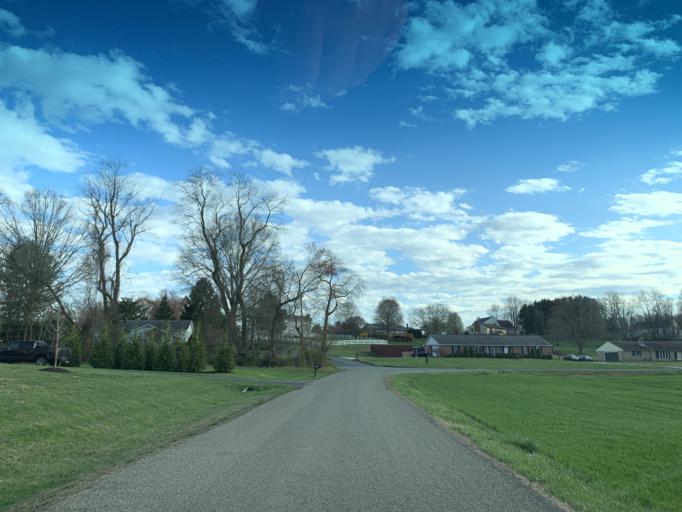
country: US
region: Maryland
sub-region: Harford County
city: South Bel Air
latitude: 39.5694
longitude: -76.2771
